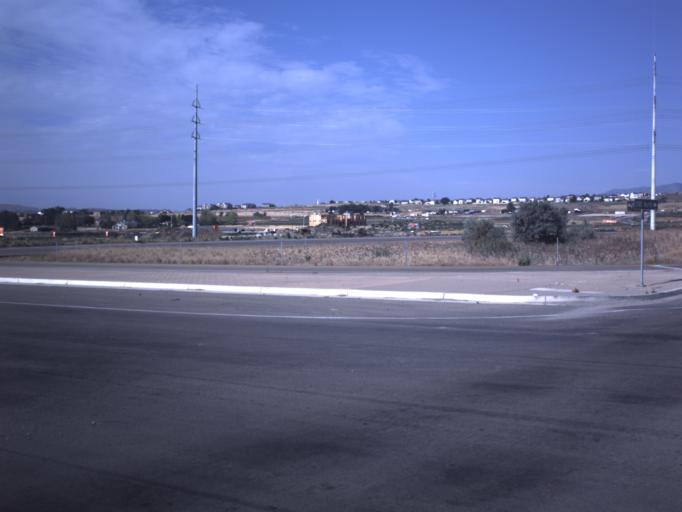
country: US
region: Utah
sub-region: Utah County
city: Lehi
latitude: 40.4132
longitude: -111.9068
